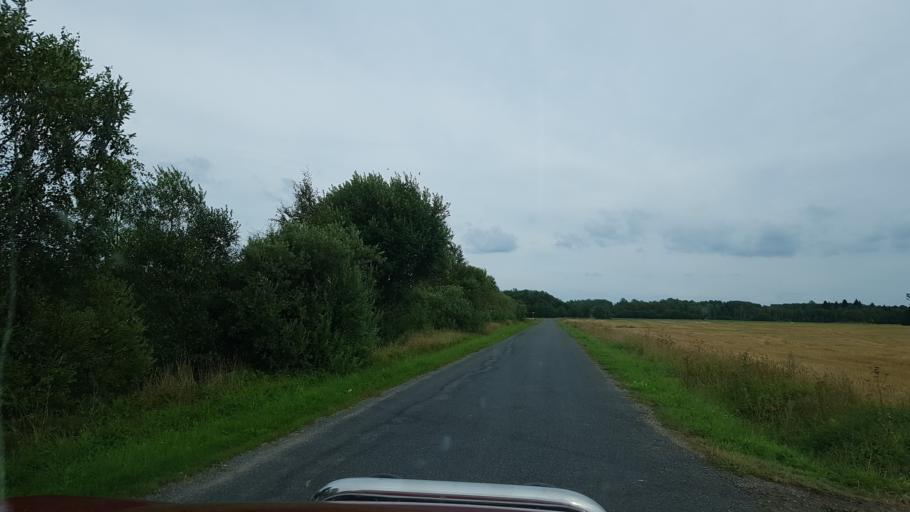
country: EE
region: Laeaene
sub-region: Ridala Parish
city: Uuemoisa
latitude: 58.9842
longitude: 23.8059
